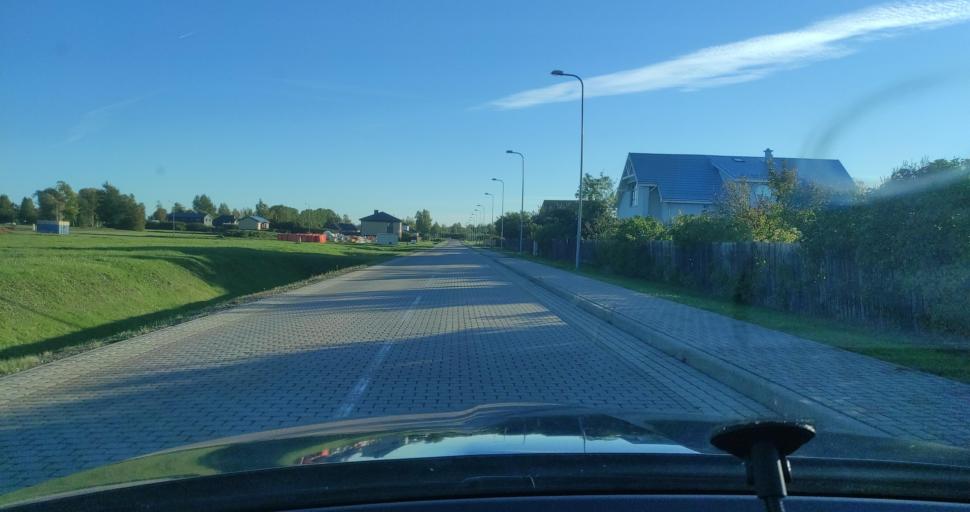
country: LV
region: Ventspils
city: Ventspils
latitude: 57.3688
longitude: 21.5748
